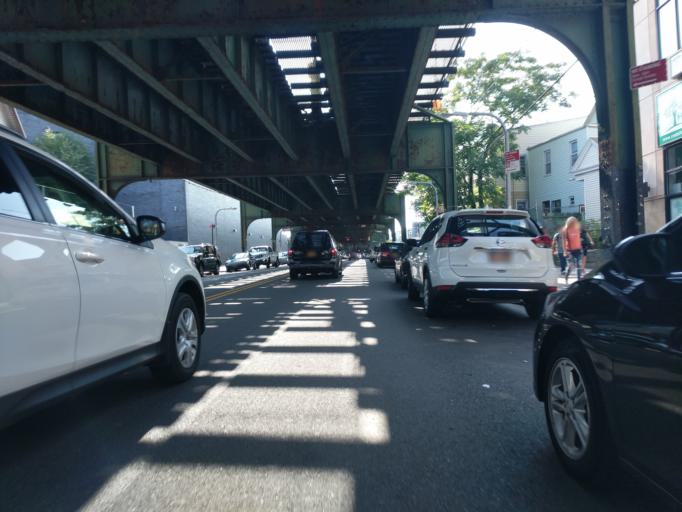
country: US
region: New York
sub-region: Queens County
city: Borough of Queens
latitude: 40.7497
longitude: -73.8649
